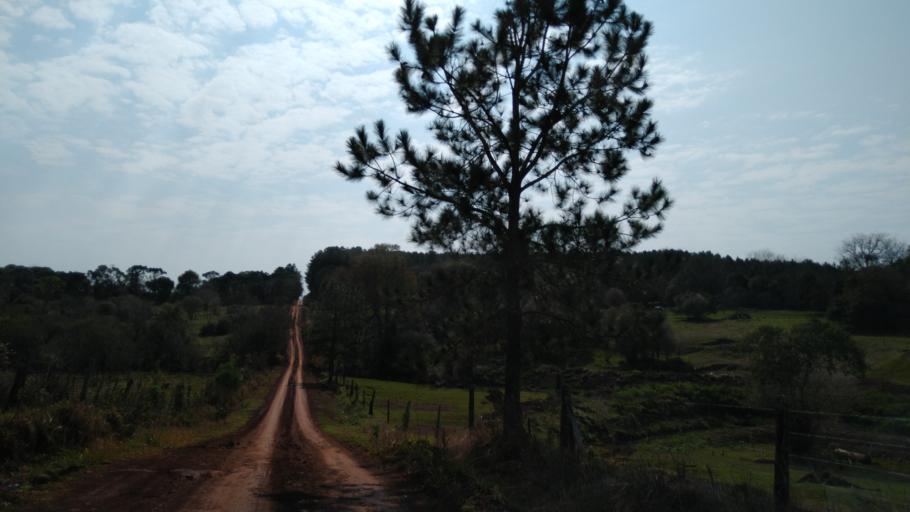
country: AR
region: Misiones
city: Capiovi
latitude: -26.9468
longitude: -55.0438
